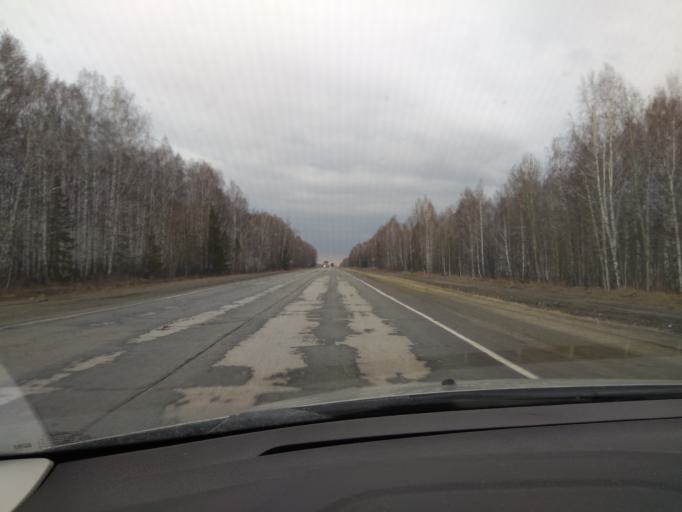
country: RU
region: Chelyabinsk
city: Tyubuk
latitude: 55.9761
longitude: 61.0402
